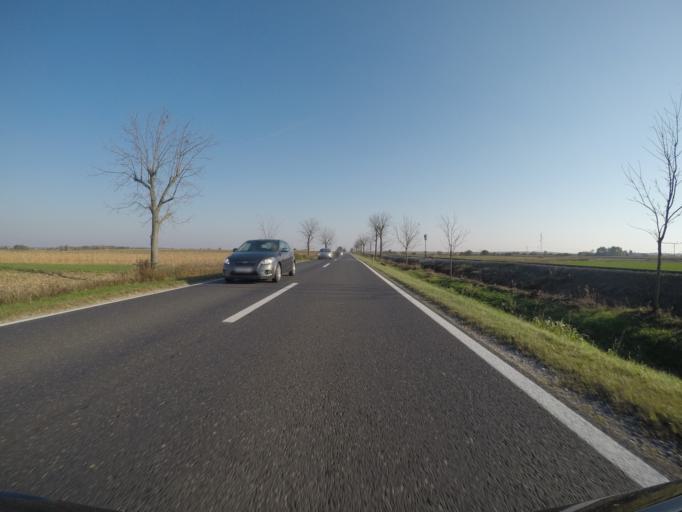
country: HR
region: Koprivnicko-Krizevacka
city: Kalinovac
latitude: 46.0193
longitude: 17.0861
